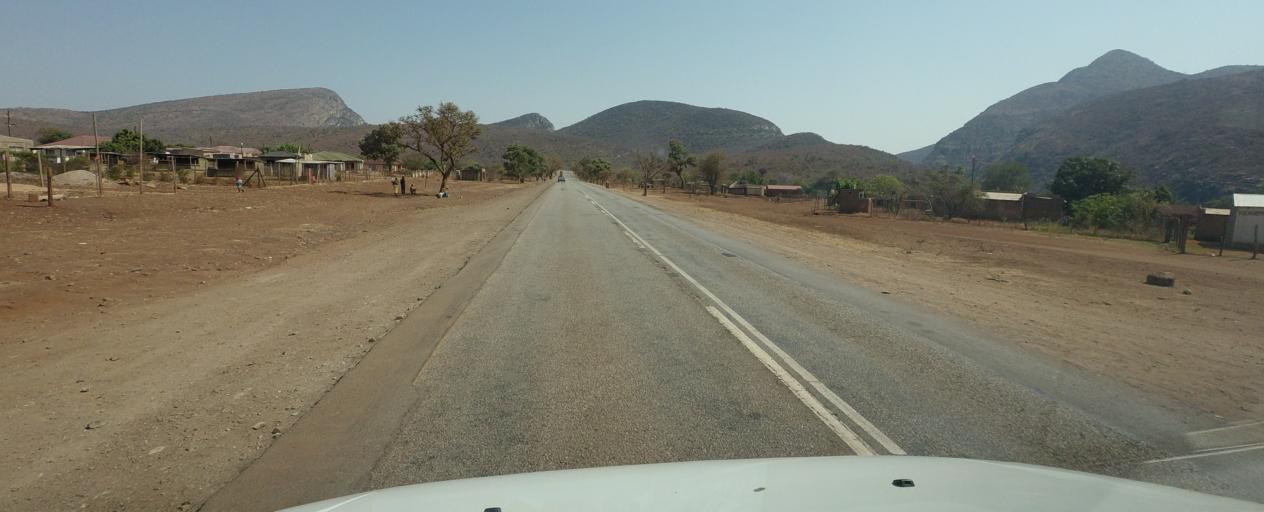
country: ZA
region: Mpumalanga
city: Burgersfort
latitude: -24.4739
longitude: 30.6058
